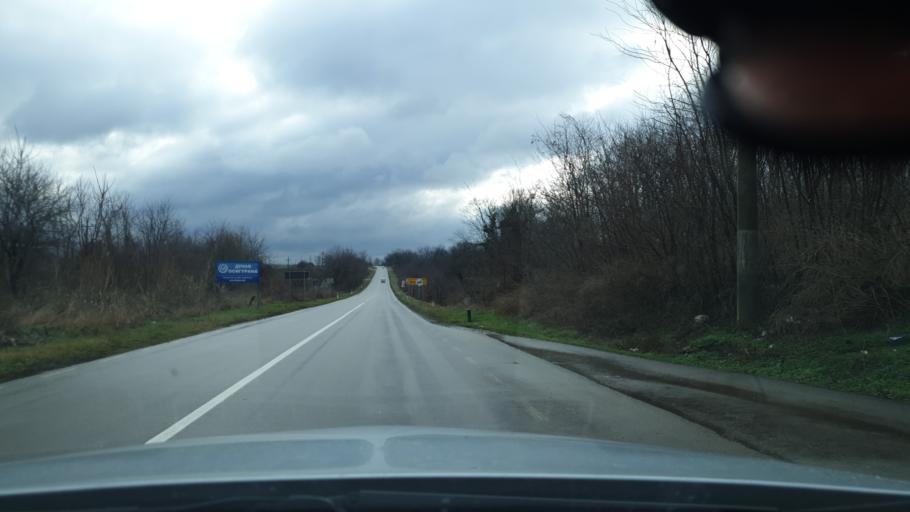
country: RS
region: Central Serbia
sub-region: Branicevski Okrug
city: Malo Crnice
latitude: 44.5596
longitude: 21.2986
